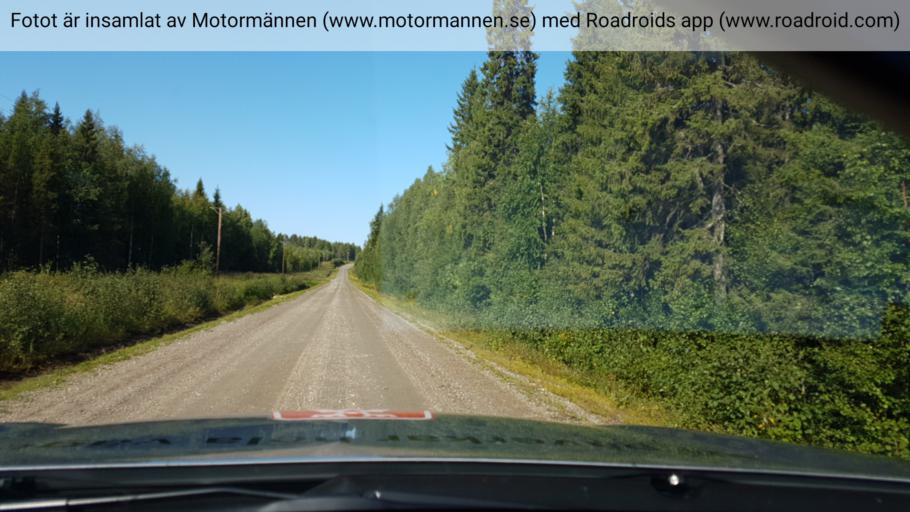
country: SE
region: Norrbotten
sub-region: Kalix Kommun
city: Kalix
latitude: 66.1339
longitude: 23.2458
